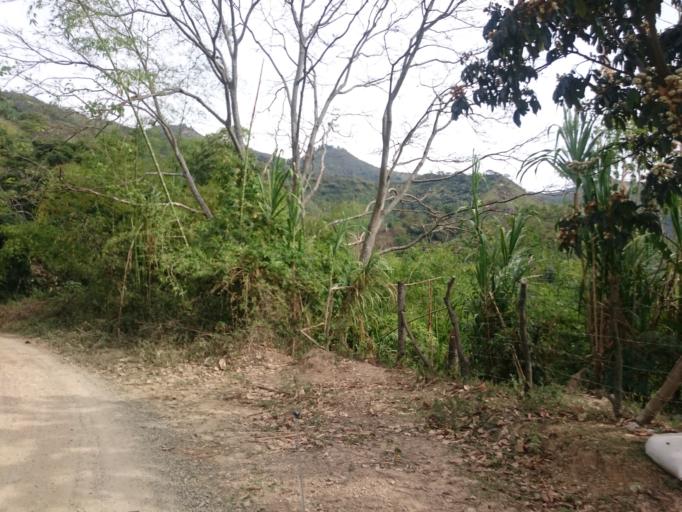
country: CO
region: Cauca
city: Suarez
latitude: 2.9322
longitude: -76.7185
